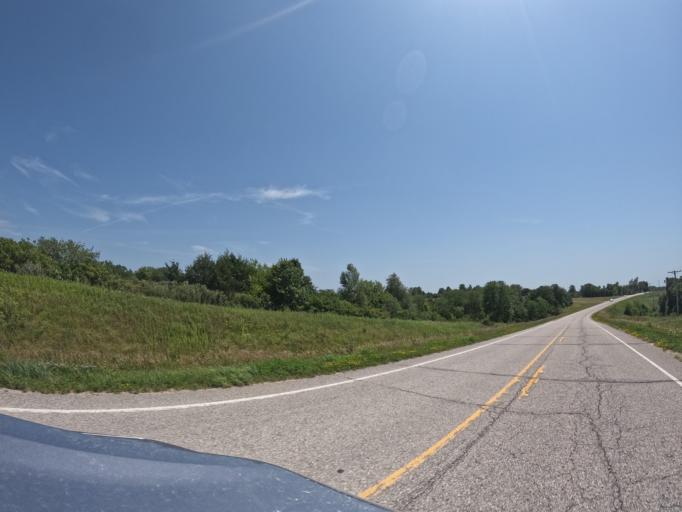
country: US
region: Iowa
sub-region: Henry County
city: Mount Pleasant
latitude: 40.9483
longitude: -91.6126
